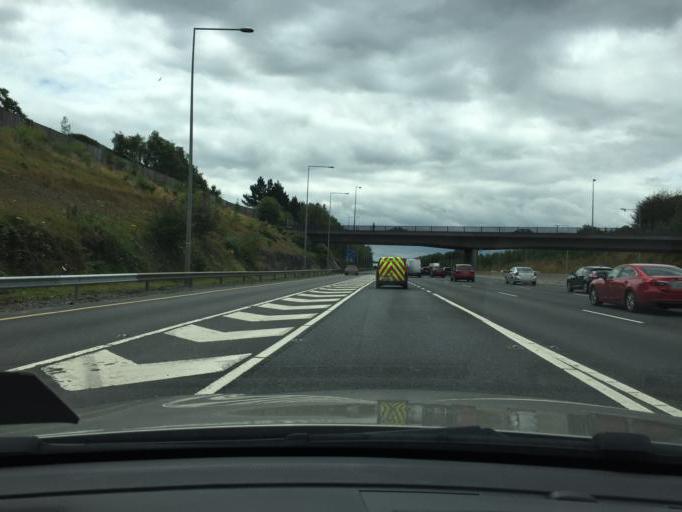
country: IE
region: Leinster
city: Castleknock
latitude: 53.3794
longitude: -6.3660
